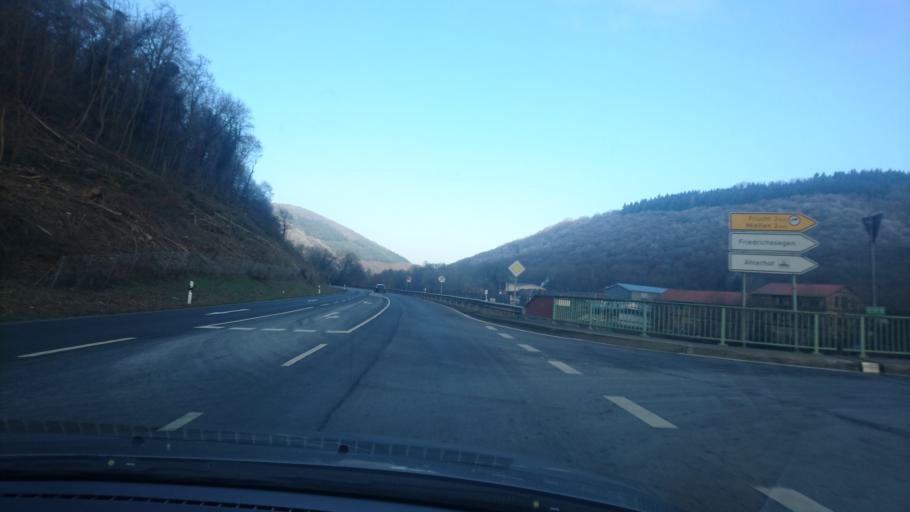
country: DE
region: Rheinland-Pfalz
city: Miellen
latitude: 50.3109
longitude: 7.6462
